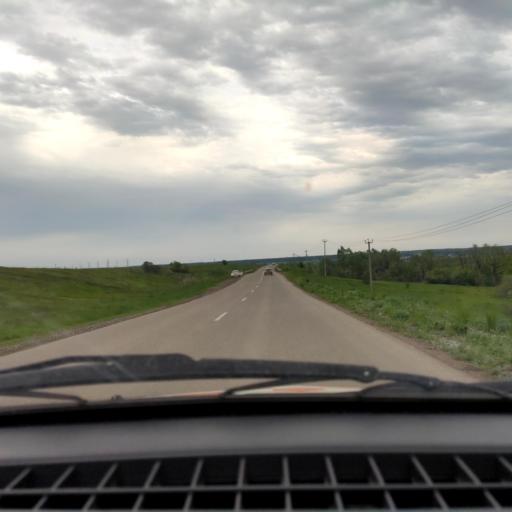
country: RU
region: Bashkortostan
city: Avdon
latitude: 54.5664
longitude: 55.7590
